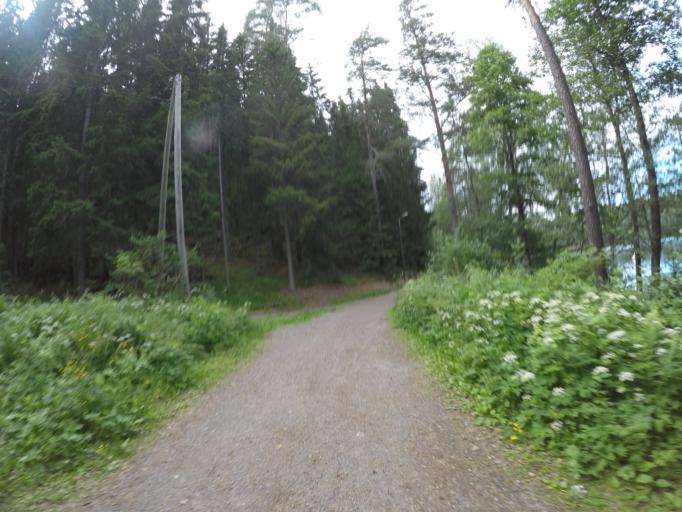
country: FI
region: Haeme
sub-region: Haemeenlinna
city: Haemeenlinna
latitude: 60.9937
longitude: 24.4173
